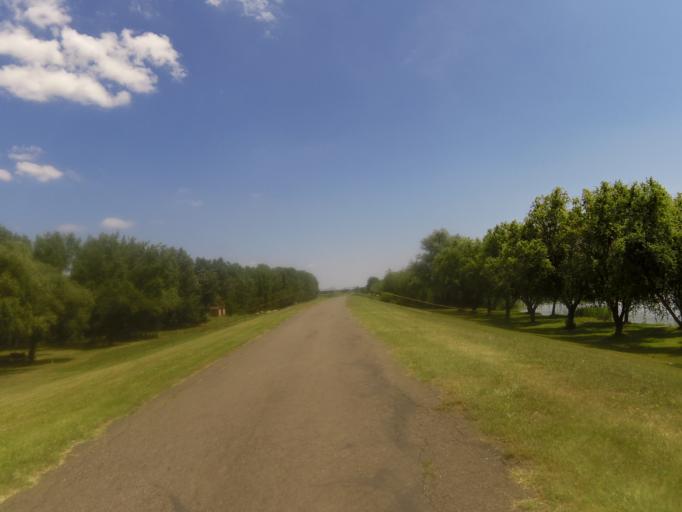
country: HU
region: Heves
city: Kiskore
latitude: 47.5058
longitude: 20.5268
